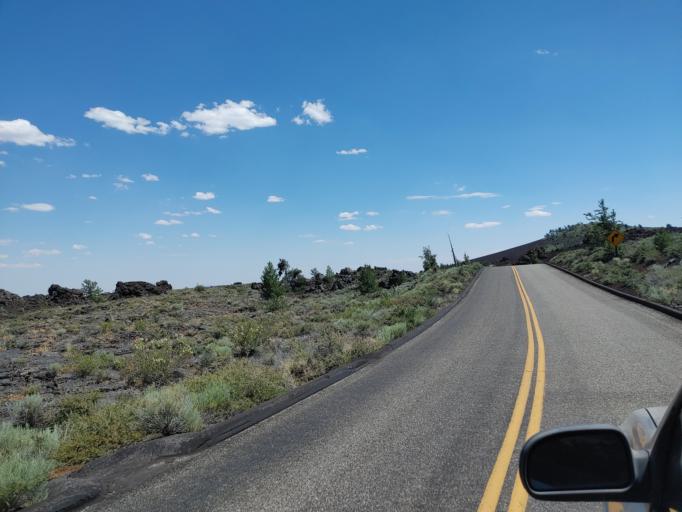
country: US
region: Idaho
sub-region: Butte County
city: Arco
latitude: 43.4592
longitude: -113.5570
